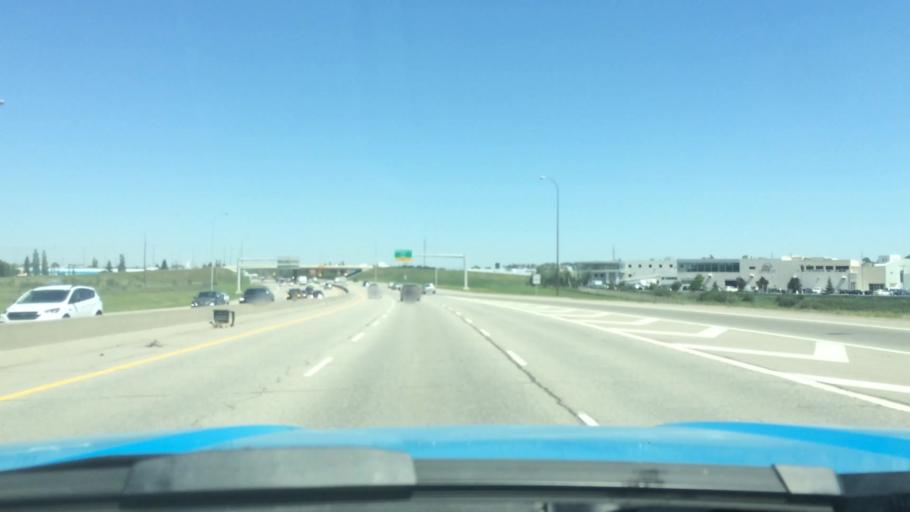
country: CA
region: Alberta
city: Calgary
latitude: 50.9832
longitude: -114.0369
